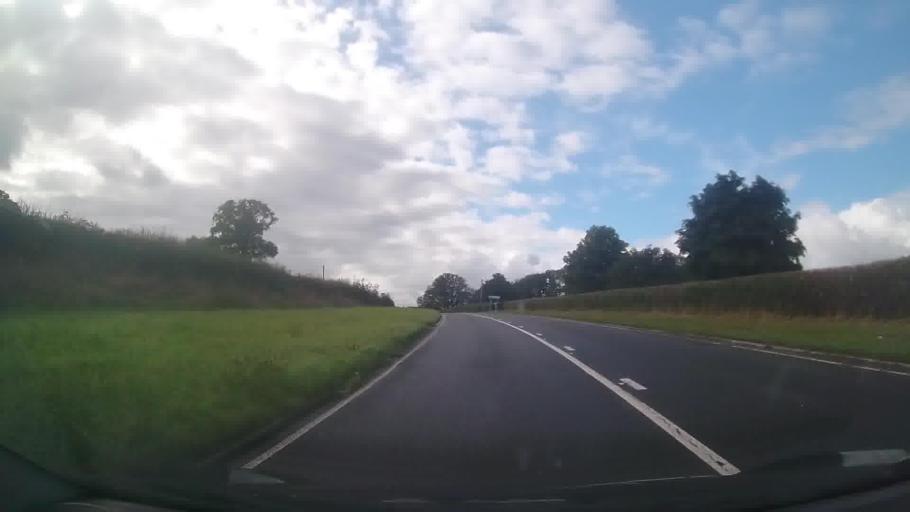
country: GB
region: Wales
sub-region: Carmarthenshire
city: Llanddarog
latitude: 51.8743
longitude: -4.1524
